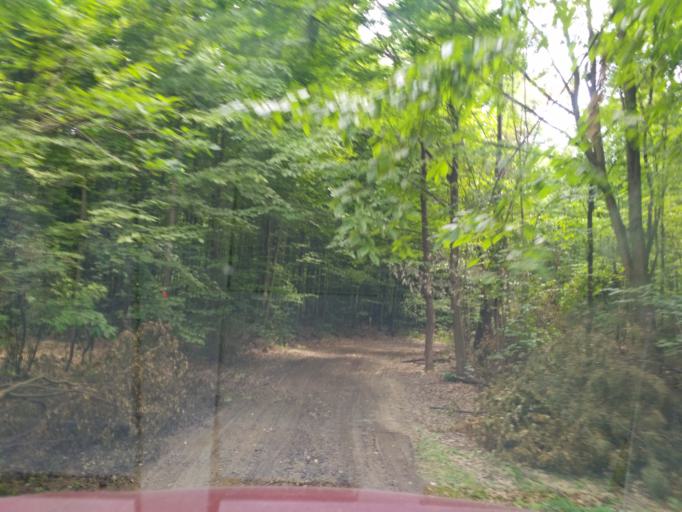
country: SK
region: Kosicky
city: Moldava nad Bodvou
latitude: 48.6580
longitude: 21.0380
